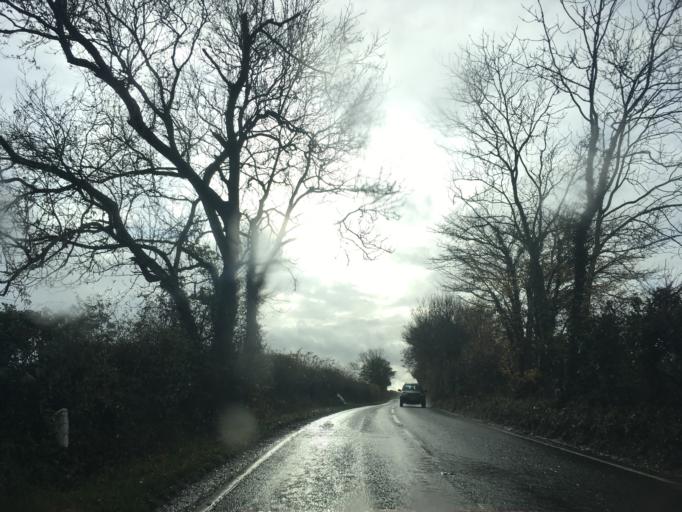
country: GB
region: England
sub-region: South Gloucestershire
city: Cold Ashton
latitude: 51.4663
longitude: -2.3686
